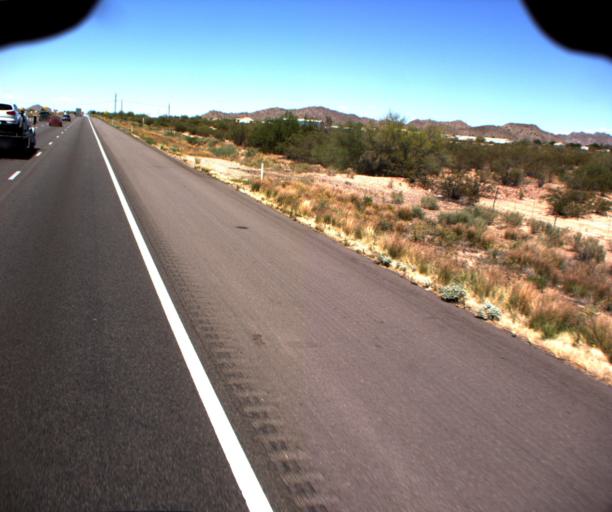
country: US
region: Arizona
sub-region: Pinal County
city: Sacaton
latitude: 32.9789
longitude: -111.7332
